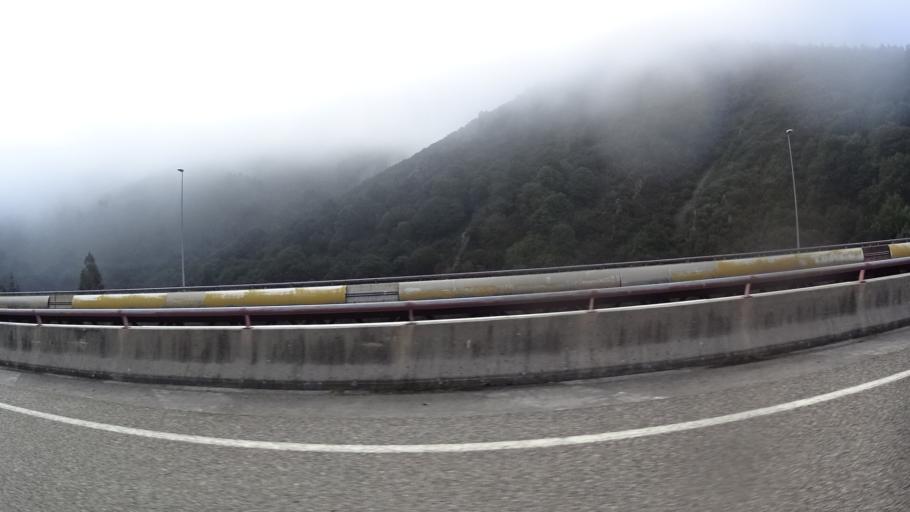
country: ES
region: Galicia
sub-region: Provincia de Lugo
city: Baralla
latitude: 42.9089
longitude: -7.2345
